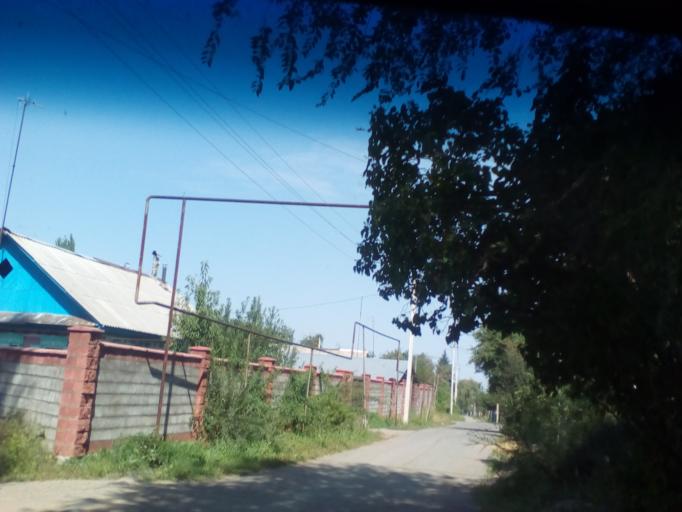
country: KZ
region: Almaty Oblysy
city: Burunday
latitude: 43.1582
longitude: 76.4082
